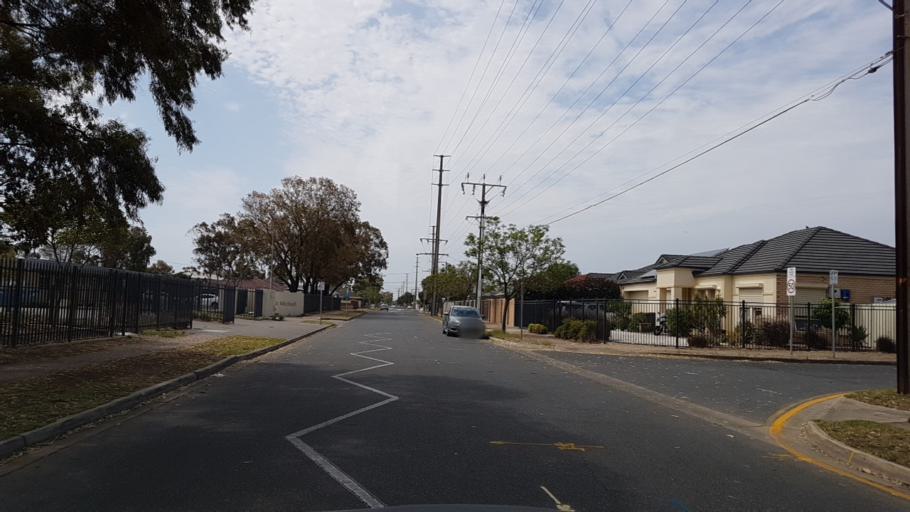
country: AU
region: South Australia
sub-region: Charles Sturt
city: Henley Beach
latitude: -34.9155
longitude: 138.5046
